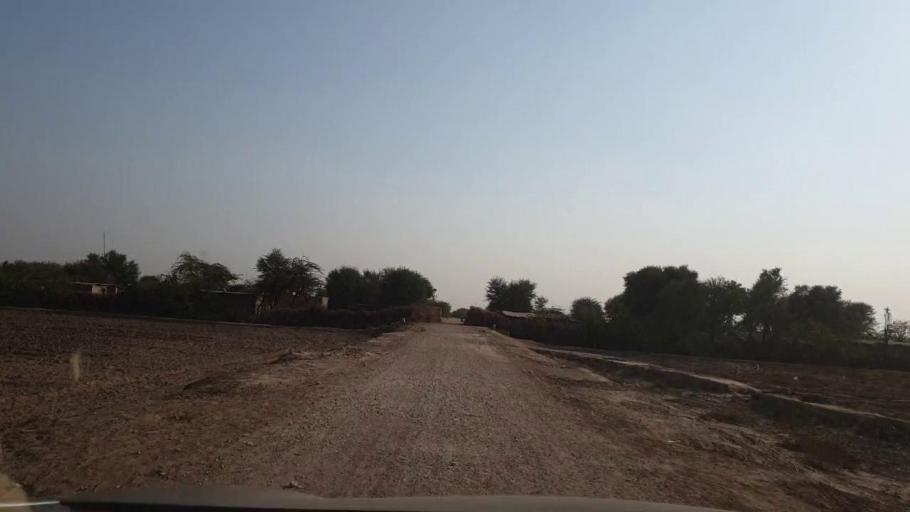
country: PK
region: Sindh
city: Tando Allahyar
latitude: 25.5069
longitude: 68.8401
